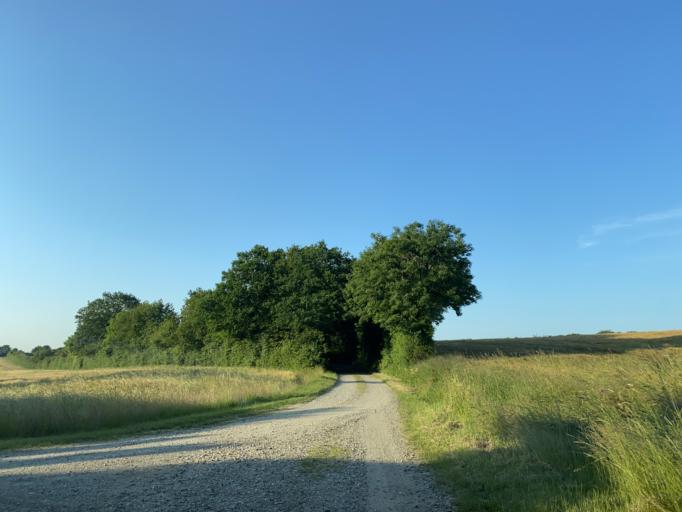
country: DK
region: South Denmark
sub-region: Haderslev Kommune
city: Starup
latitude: 55.1697
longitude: 9.5135
